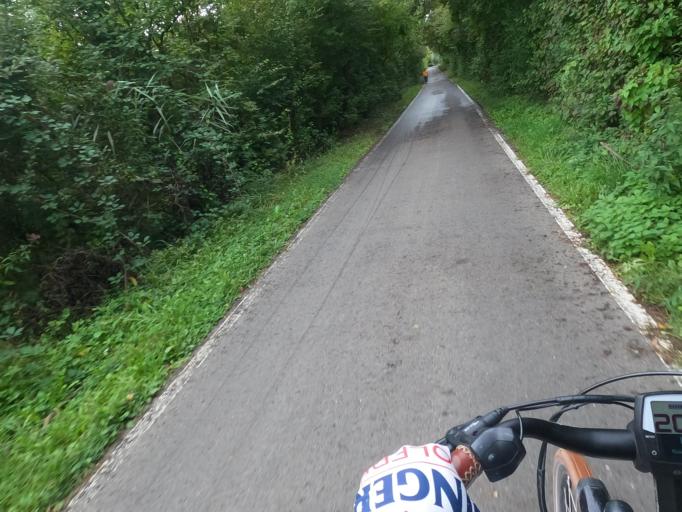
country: CH
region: Thurgau
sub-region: Kreuzlingen District
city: Ermatingen
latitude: 47.6994
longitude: 9.1096
